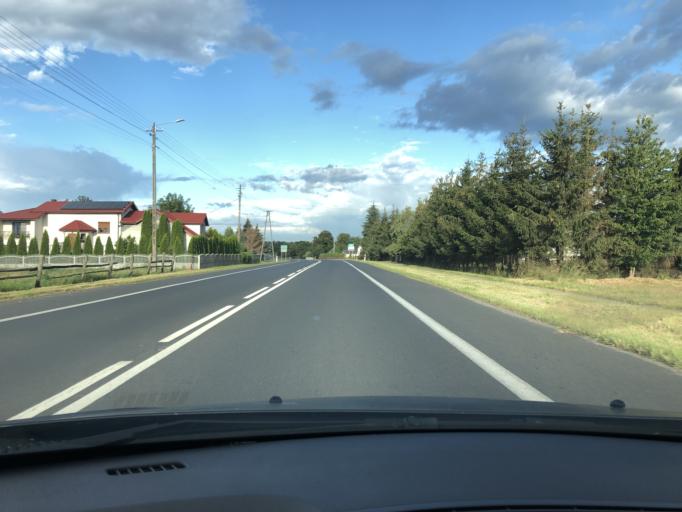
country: PL
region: Lodz Voivodeship
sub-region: Powiat wieruszowski
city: Sokolniki
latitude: 51.3049
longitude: 18.3138
